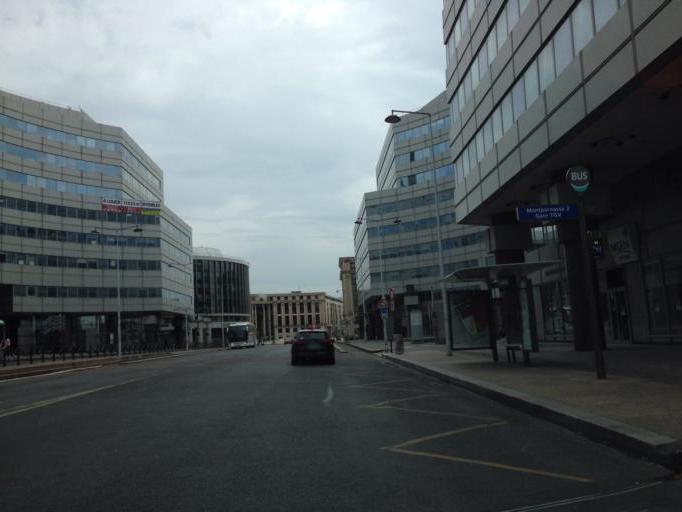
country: FR
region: Ile-de-France
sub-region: Departement des Hauts-de-Seine
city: Montrouge
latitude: 48.8389
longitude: 2.3166
